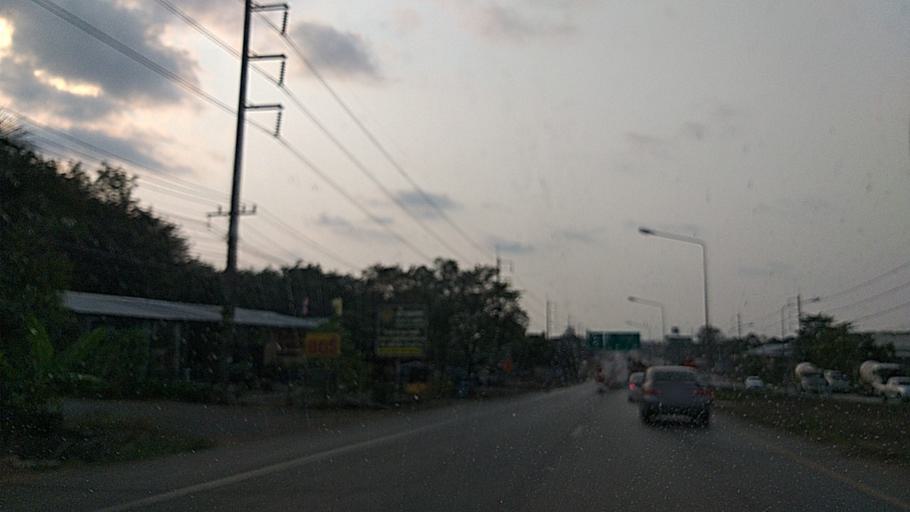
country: TH
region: Trat
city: Khao Saming
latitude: 12.3684
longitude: 102.3925
